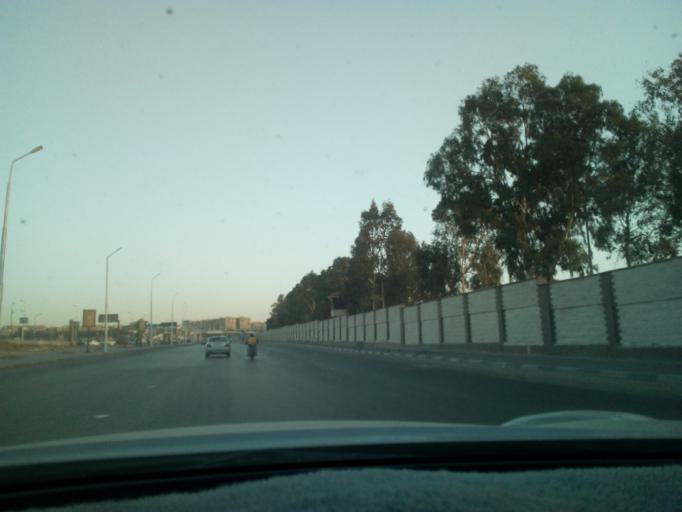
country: EG
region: Muhafazat al Qalyubiyah
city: Al Khankah
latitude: 30.1147
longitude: 31.3662
